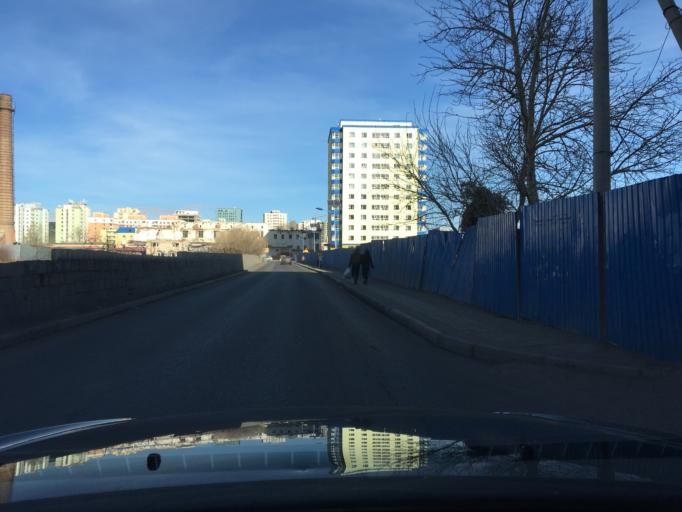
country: MN
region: Ulaanbaatar
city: Ulaanbaatar
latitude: 47.8918
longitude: 106.8964
